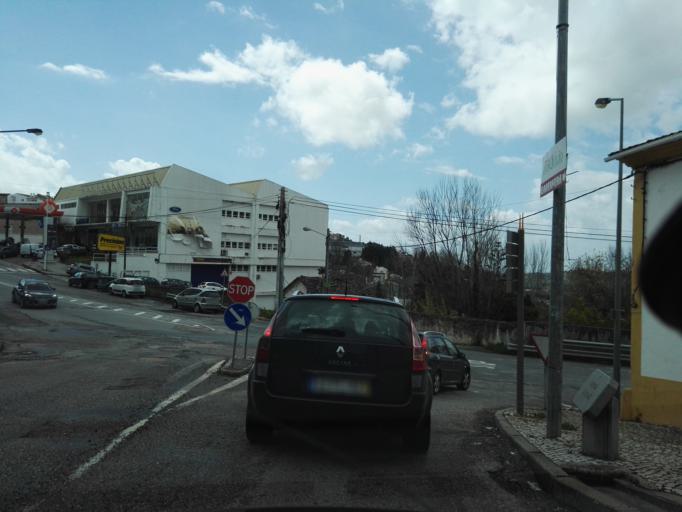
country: PT
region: Portalegre
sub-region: Portalegre
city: Portalegre
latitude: 39.2968
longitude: -7.4327
